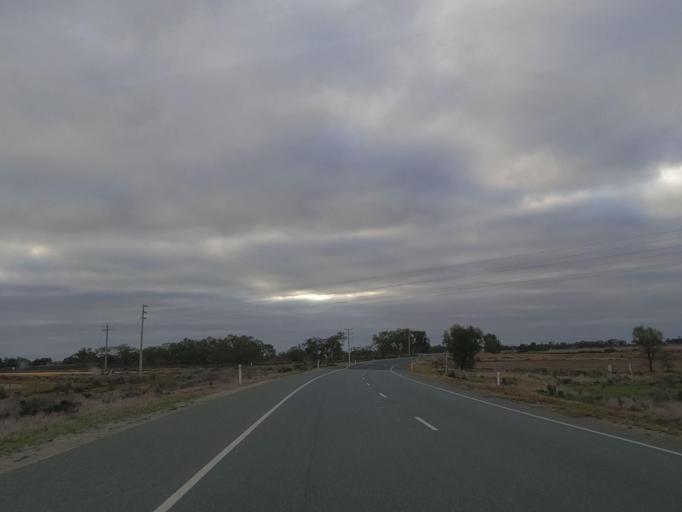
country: AU
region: Victoria
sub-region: Swan Hill
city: Swan Hill
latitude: -35.6224
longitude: 143.8042
